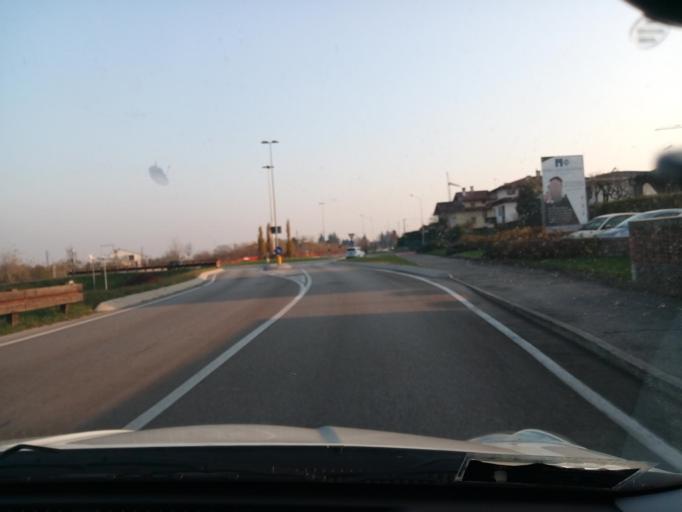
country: IT
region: Veneto
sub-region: Provincia di Vicenza
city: Schio
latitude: 45.7050
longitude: 11.3615
